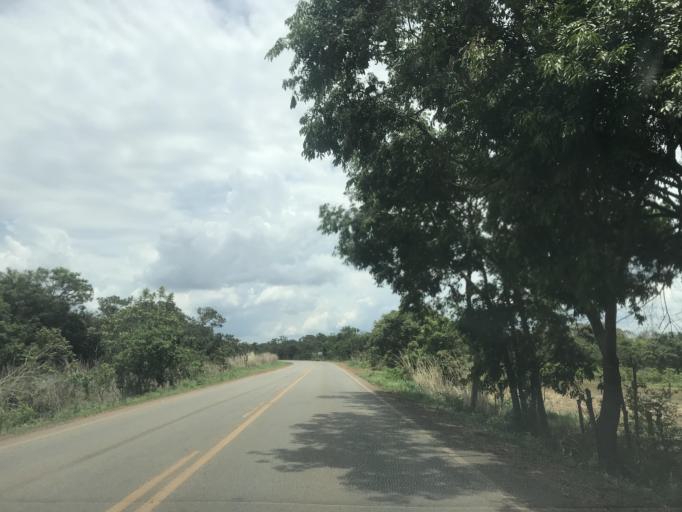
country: BR
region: Goias
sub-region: Vianopolis
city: Vianopolis
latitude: -16.7318
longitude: -48.4439
